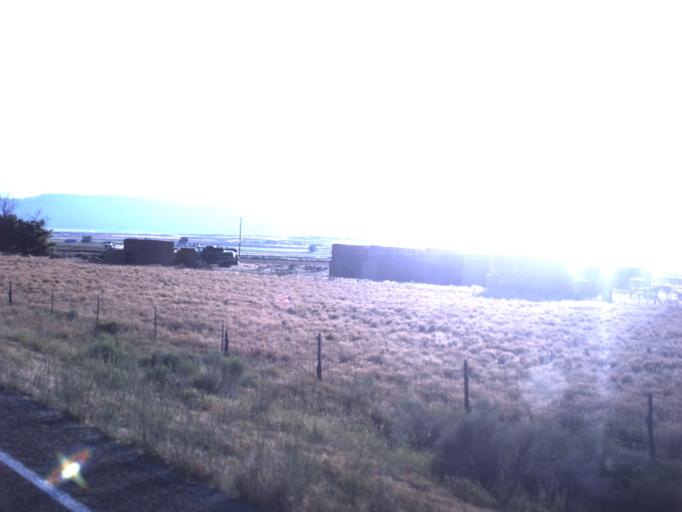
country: US
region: Utah
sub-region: Sanpete County
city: Mount Pleasant
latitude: 39.5143
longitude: -111.4913
